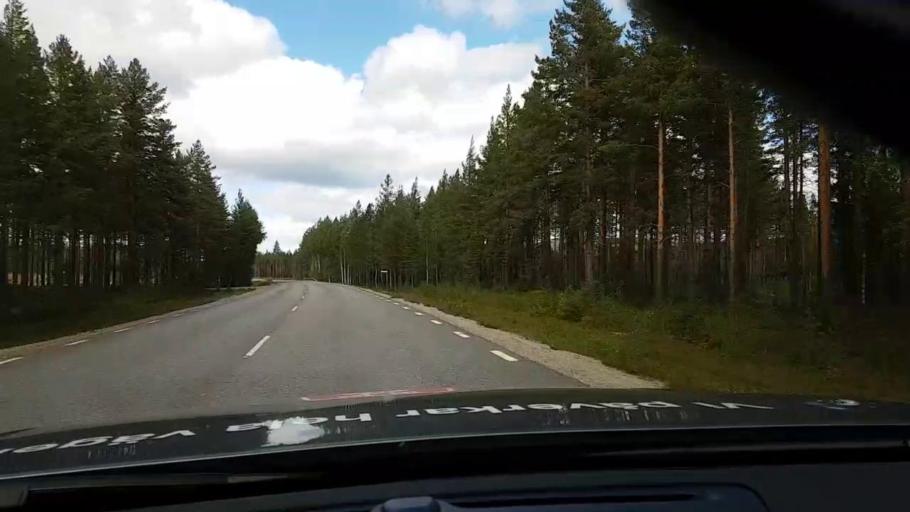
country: SE
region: Vaesternorrland
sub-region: OErnskoeldsviks Kommun
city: Bredbyn
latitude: 63.5361
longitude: 17.9653
